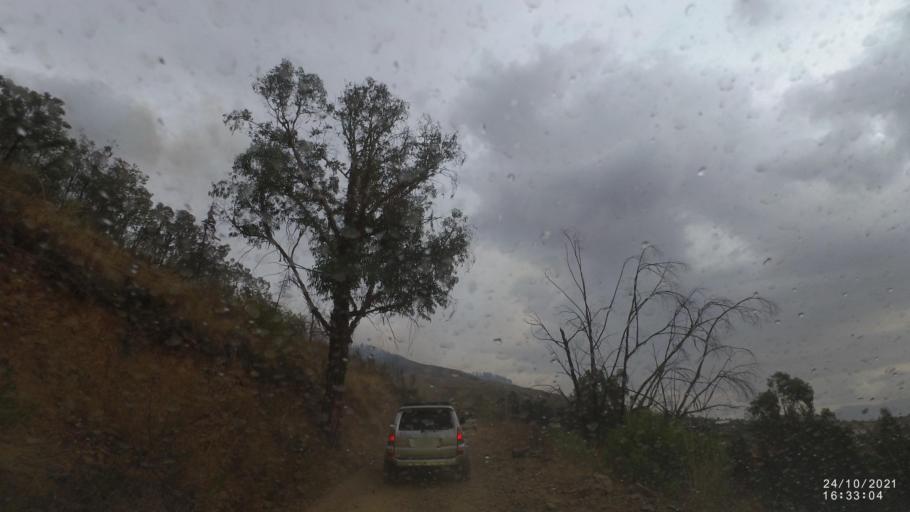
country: BO
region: Cochabamba
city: Cochabamba
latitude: -17.3478
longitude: -66.1488
